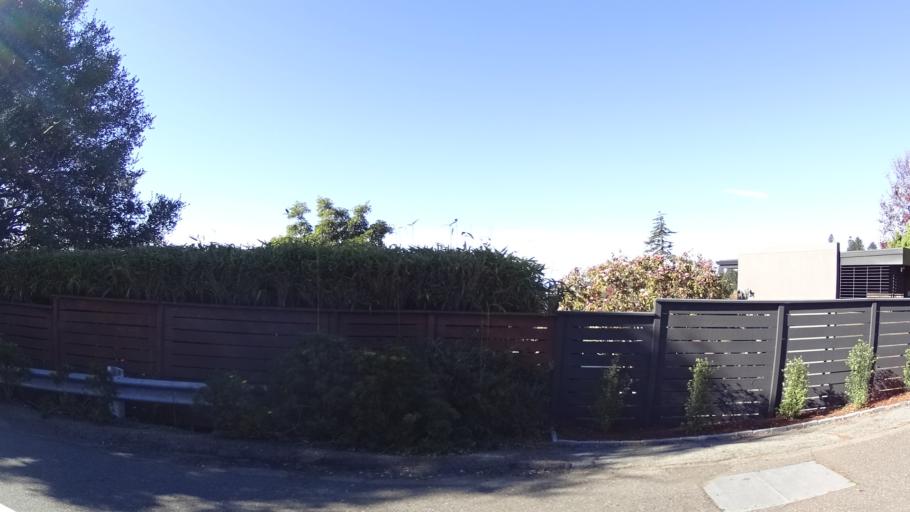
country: US
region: California
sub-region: Alameda County
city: Piedmont
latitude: 37.8231
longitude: -122.2150
